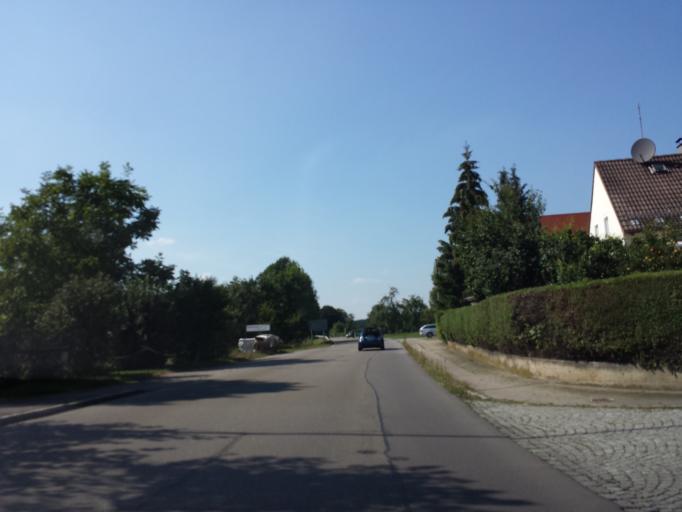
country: DE
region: Bavaria
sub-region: Swabia
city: Pfaffenhausen
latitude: 48.1189
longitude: 10.4509
